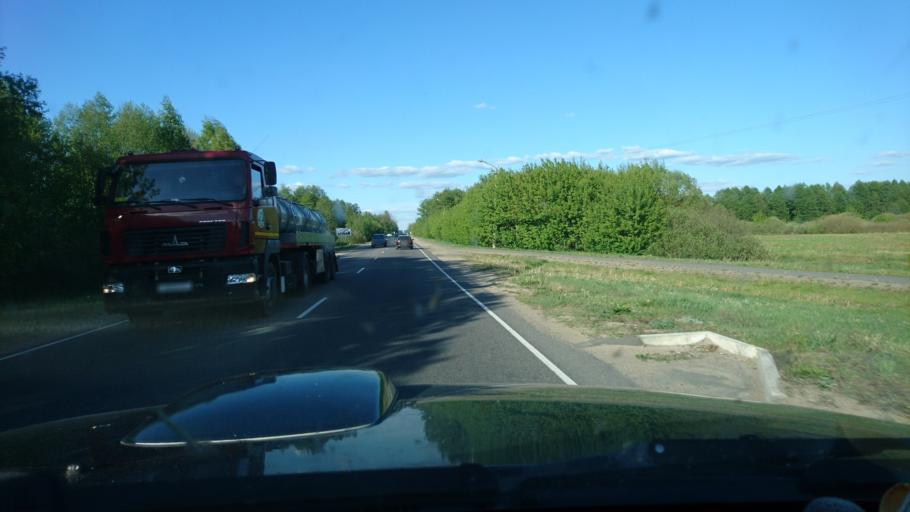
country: BY
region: Brest
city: Byaroza
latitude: 52.5429
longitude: 25.0021
